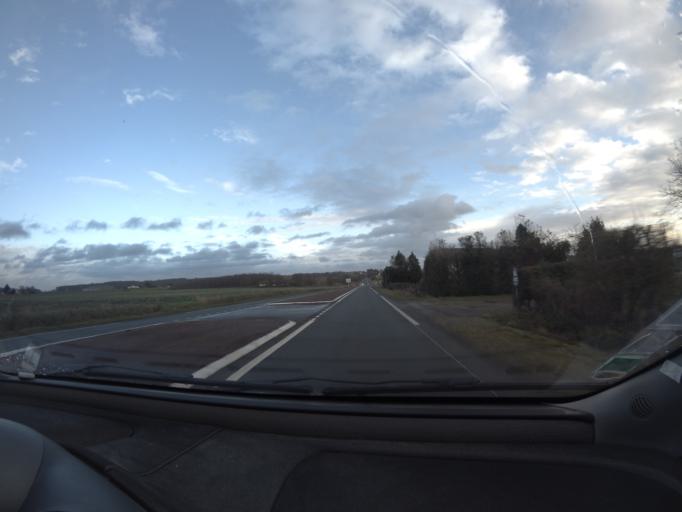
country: FR
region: Pays de la Loire
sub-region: Departement de la Sarthe
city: La Milesse
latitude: 48.0710
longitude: 0.1391
